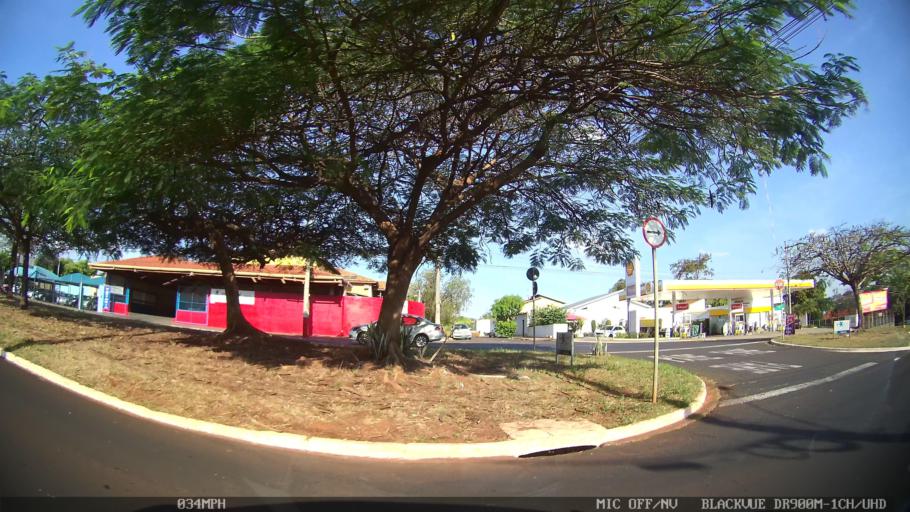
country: BR
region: Sao Paulo
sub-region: Ribeirao Preto
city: Ribeirao Preto
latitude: -21.2109
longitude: -47.7726
